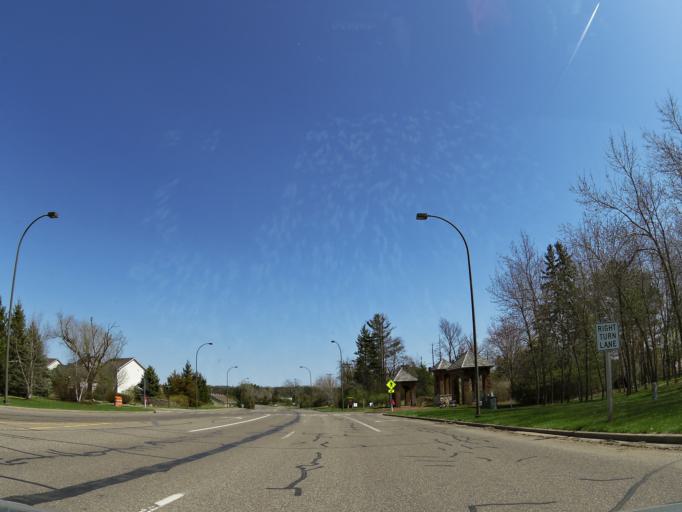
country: US
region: Wisconsin
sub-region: Saint Croix County
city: Hudson
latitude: 44.9594
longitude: -92.7024
